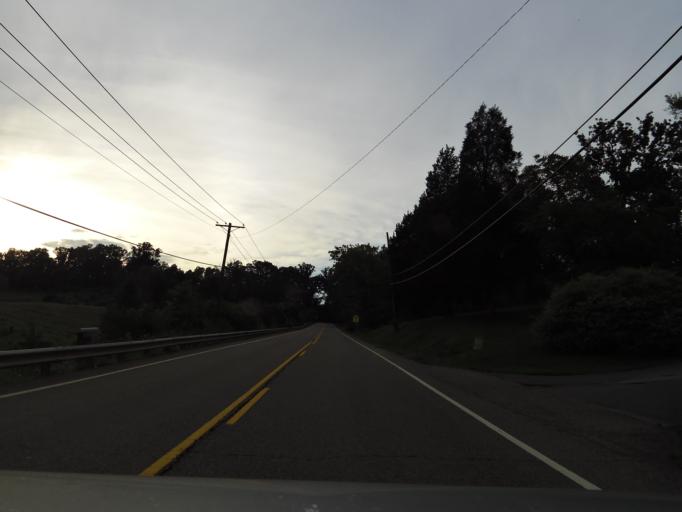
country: US
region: Tennessee
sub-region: Knox County
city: Knoxville
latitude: 35.9020
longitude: -83.9378
